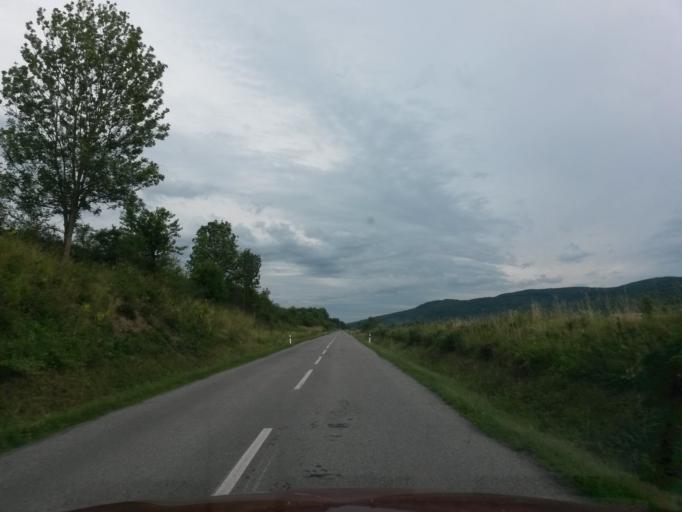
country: SK
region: Banskobystricky
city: Detva
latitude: 48.4088
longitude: 19.3692
